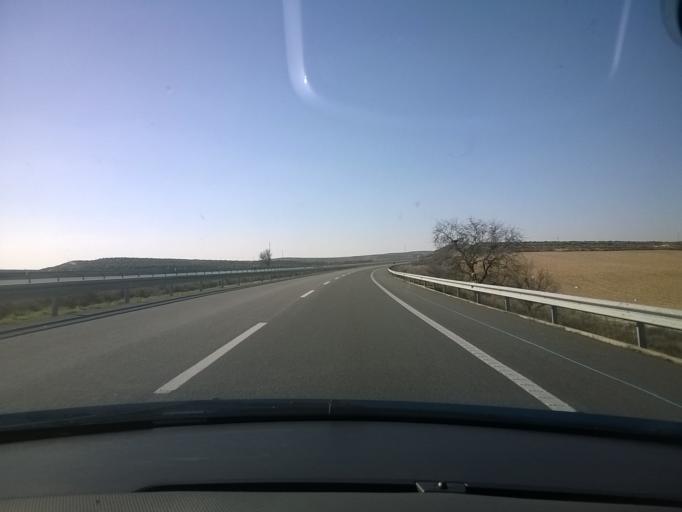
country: ES
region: Aragon
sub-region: Provincia de Huesca
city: Candasnos
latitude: 41.5106
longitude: 0.0189
